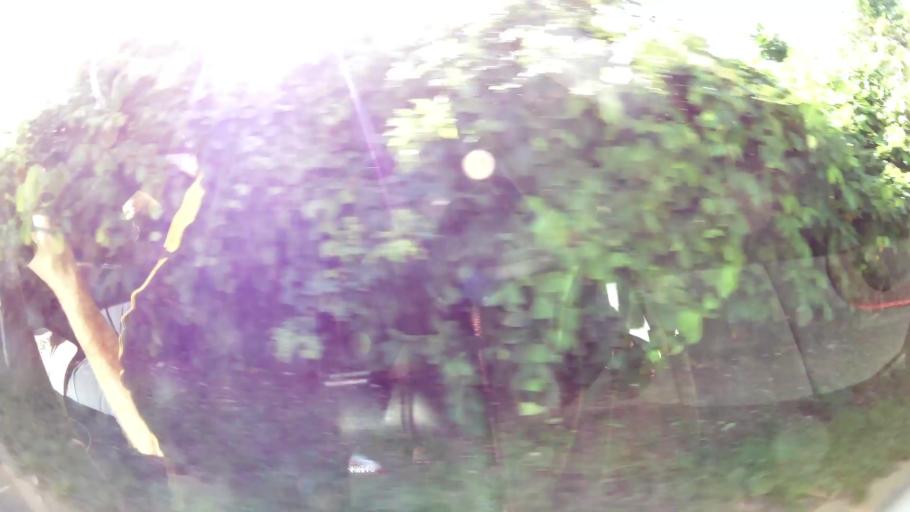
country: GF
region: Guyane
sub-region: Guyane
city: Remire-Montjoly
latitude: 4.9176
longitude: -52.2688
